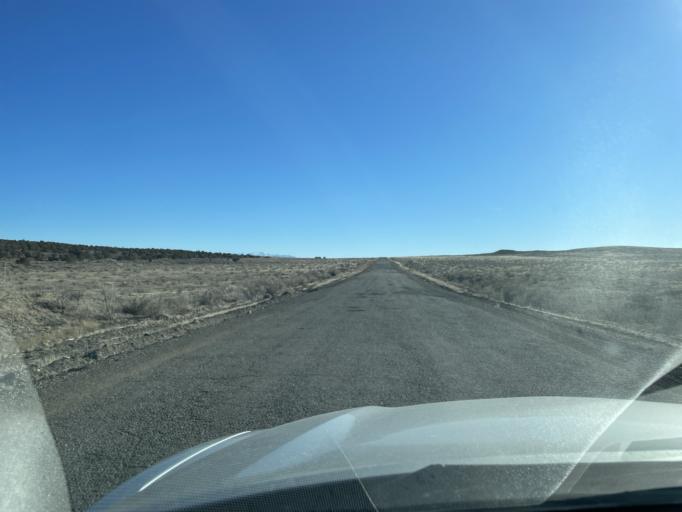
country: US
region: Colorado
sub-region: Mesa County
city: Loma
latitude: 39.1876
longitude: -109.1268
